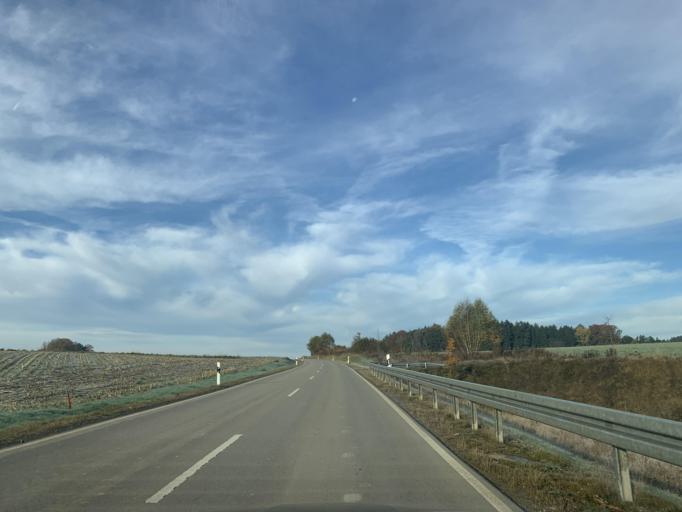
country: DE
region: Bavaria
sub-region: Upper Palatinate
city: Thanstein
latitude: 49.4033
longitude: 12.4564
